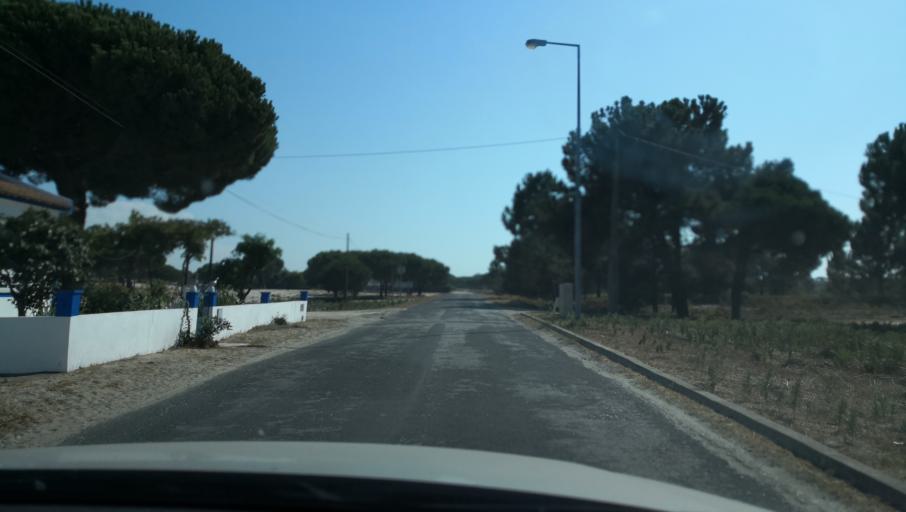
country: PT
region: Setubal
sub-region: Setubal
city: Setubal
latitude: 38.4048
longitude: -8.7545
